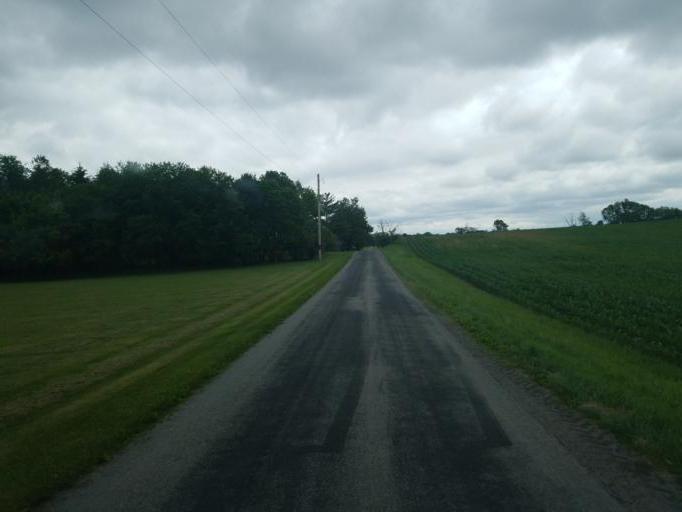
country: US
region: Ohio
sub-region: Wyandot County
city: Upper Sandusky
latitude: 40.7675
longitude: -83.2152
